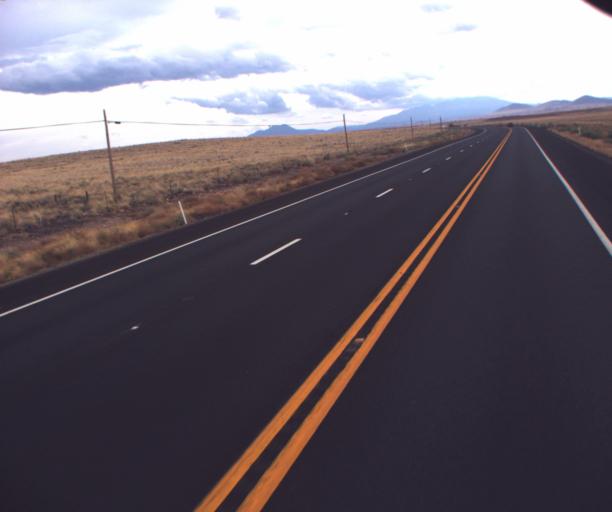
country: US
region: Arizona
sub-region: Coconino County
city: Tuba City
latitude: 35.6938
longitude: -111.5027
